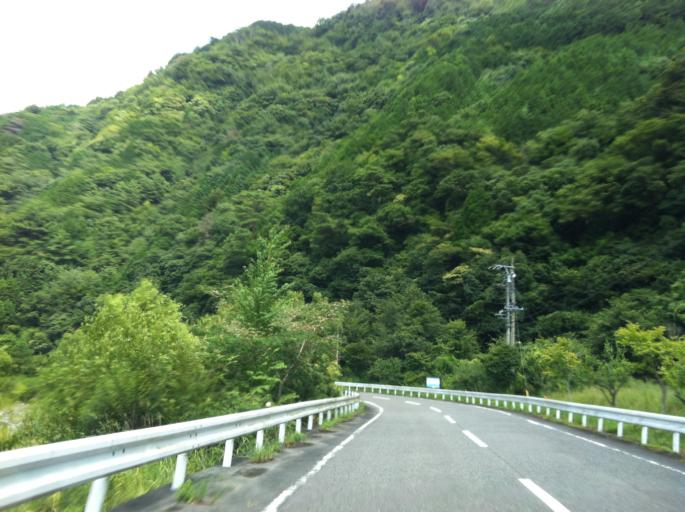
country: JP
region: Shizuoka
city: Shizuoka-shi
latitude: 35.2515
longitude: 138.3394
